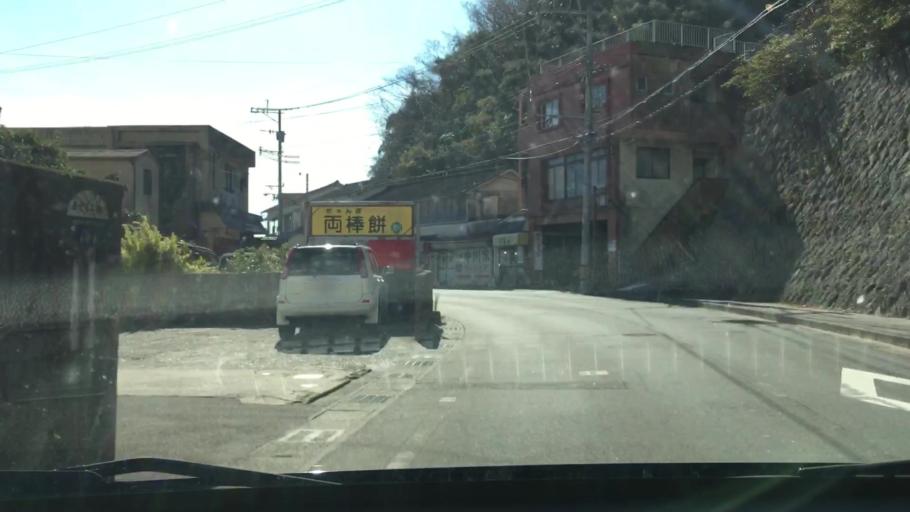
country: JP
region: Kagoshima
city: Kagoshima-shi
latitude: 31.6134
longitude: 130.5747
